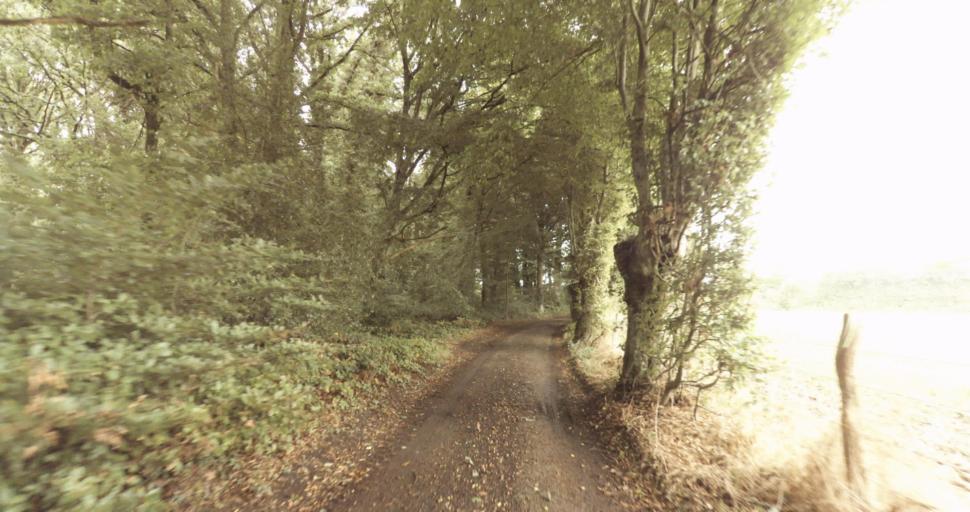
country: FR
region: Lower Normandy
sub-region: Departement de l'Orne
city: Vimoutiers
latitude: 48.8883
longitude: 0.1989
